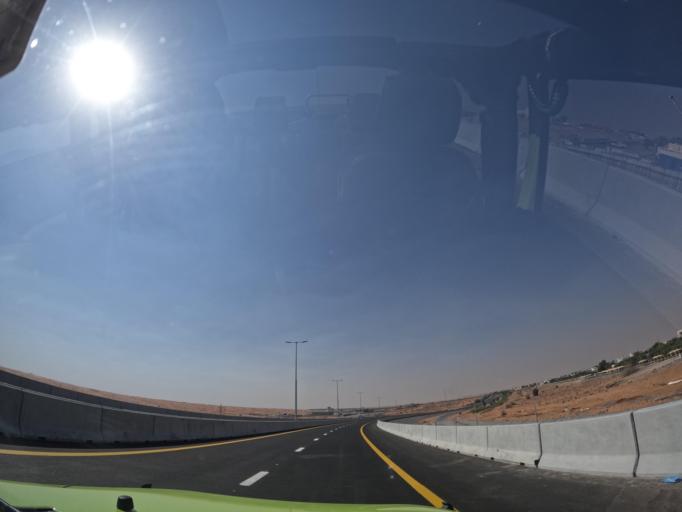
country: OM
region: Al Buraimi
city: Al Buraymi
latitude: 24.7427
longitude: 55.8000
